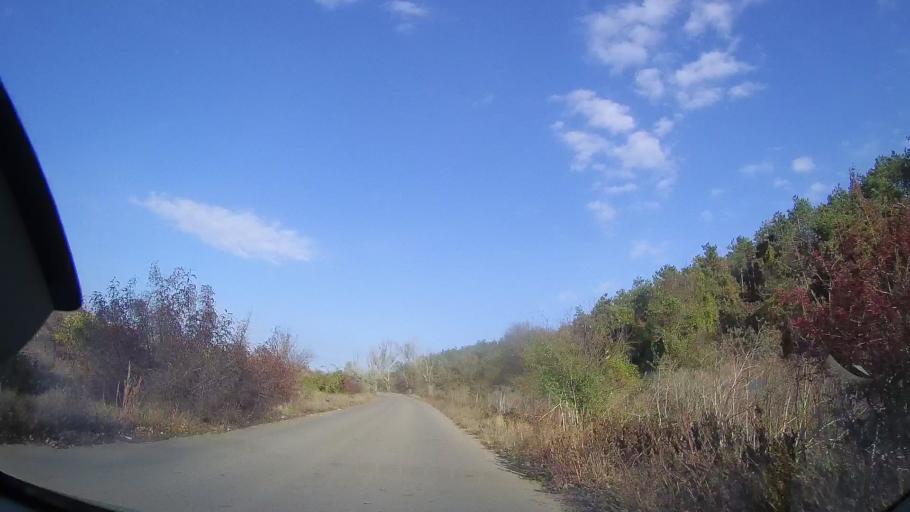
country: RO
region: Constanta
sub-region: Comuna Limanu
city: Limanu
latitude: 43.8195
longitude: 28.5194
